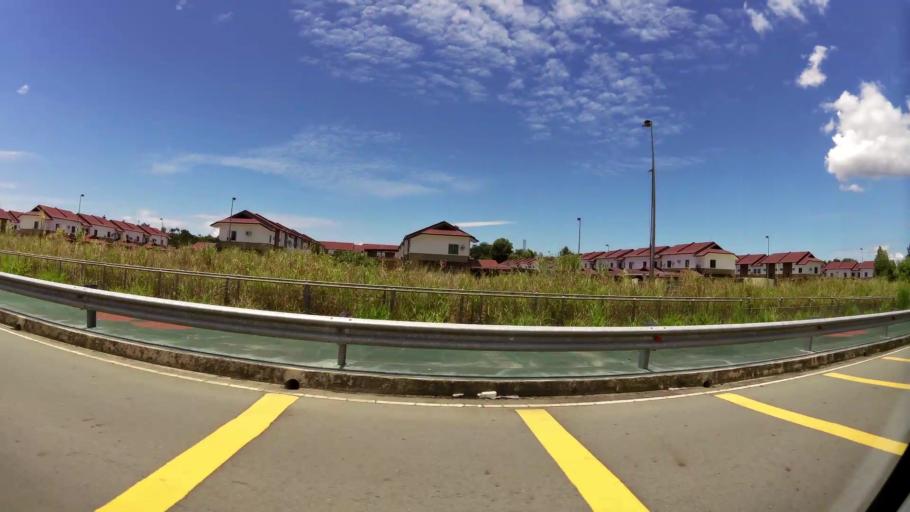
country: BN
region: Brunei and Muara
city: Bandar Seri Begawan
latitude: 5.0057
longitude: 115.0209
